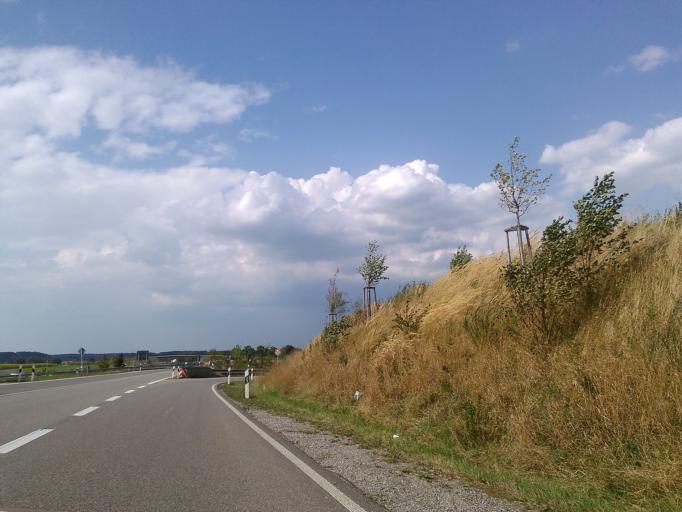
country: DE
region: Bavaria
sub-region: Upper Bavaria
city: Puchheim
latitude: 48.1469
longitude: 11.3400
